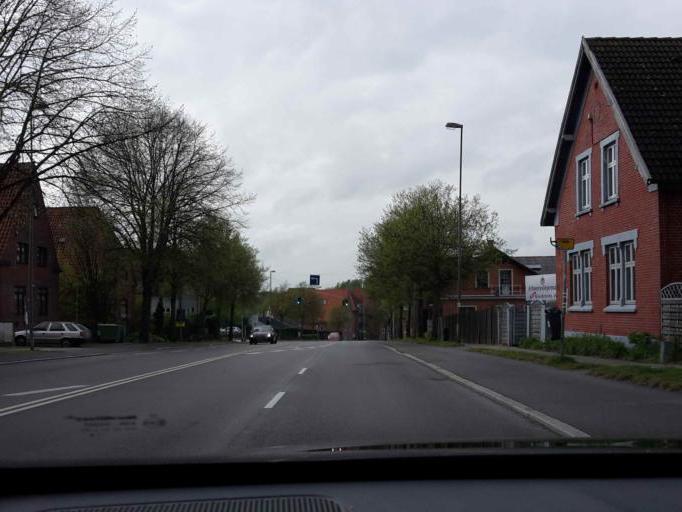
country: DK
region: South Denmark
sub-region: Odense Kommune
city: Odense
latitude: 55.4001
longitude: 10.3593
